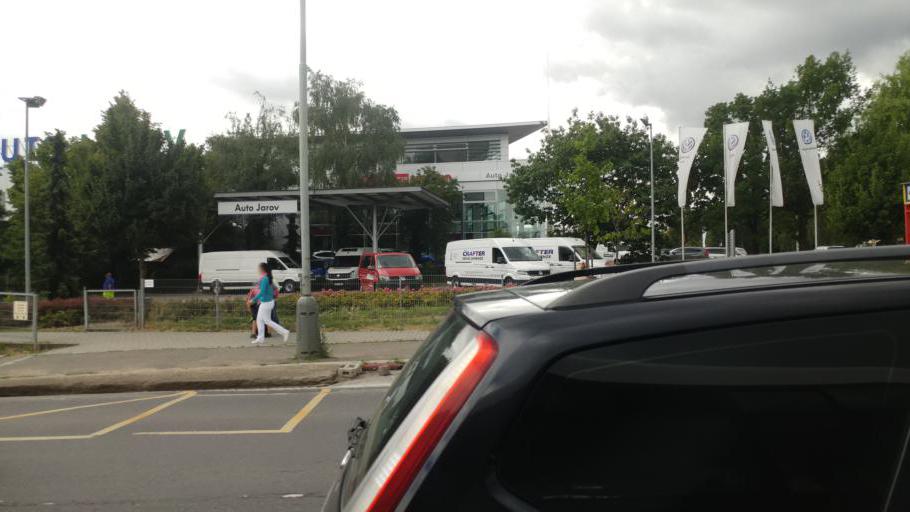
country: CZ
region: Praha
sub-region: Praha 9
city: Vysocany
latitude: 50.0913
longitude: 14.4998
